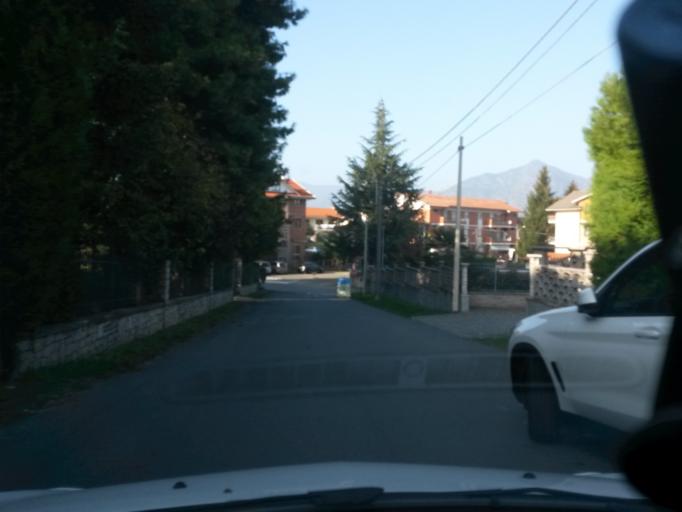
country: IT
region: Piedmont
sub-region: Provincia di Torino
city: Buttigliera Alta
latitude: 45.0676
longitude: 7.4311
